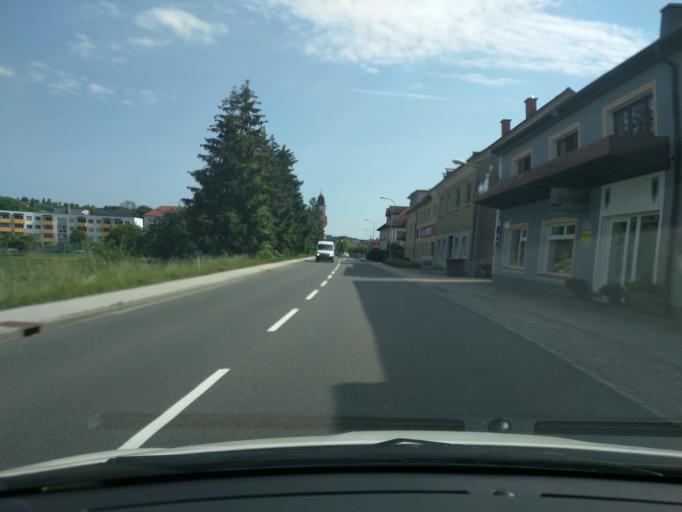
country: AT
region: Lower Austria
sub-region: Politischer Bezirk Amstetten
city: Sonntagberg
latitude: 48.0125
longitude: 14.7450
